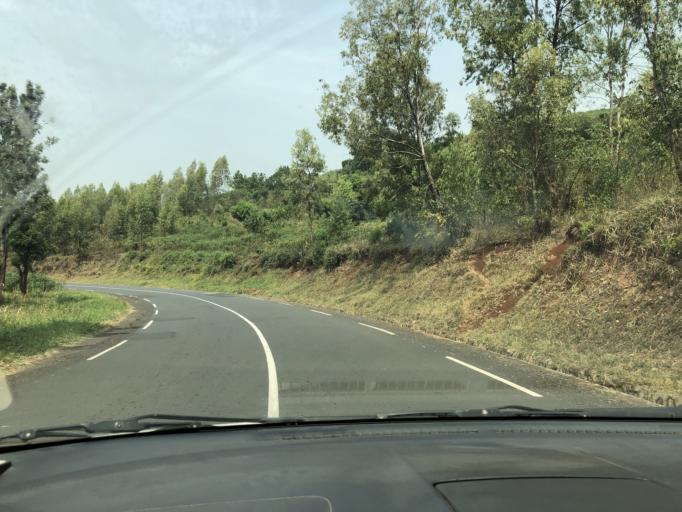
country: RW
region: Western Province
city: Cyangugu
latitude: -2.6694
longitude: 29.0019
